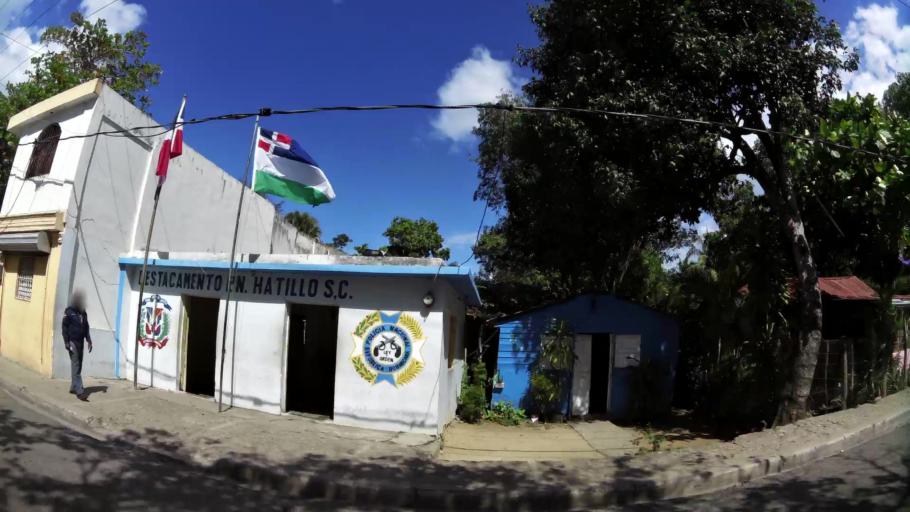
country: DO
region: San Cristobal
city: San Cristobal
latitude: 18.4271
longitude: -70.0849
